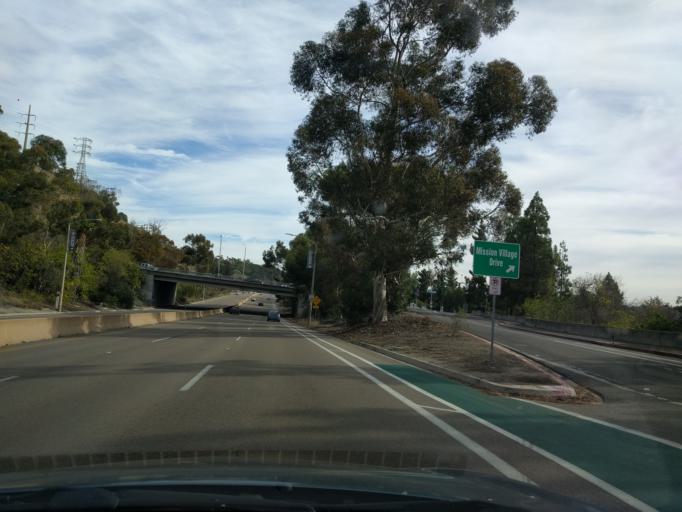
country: US
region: California
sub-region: San Diego County
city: San Diego
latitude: 32.7863
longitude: -117.1215
